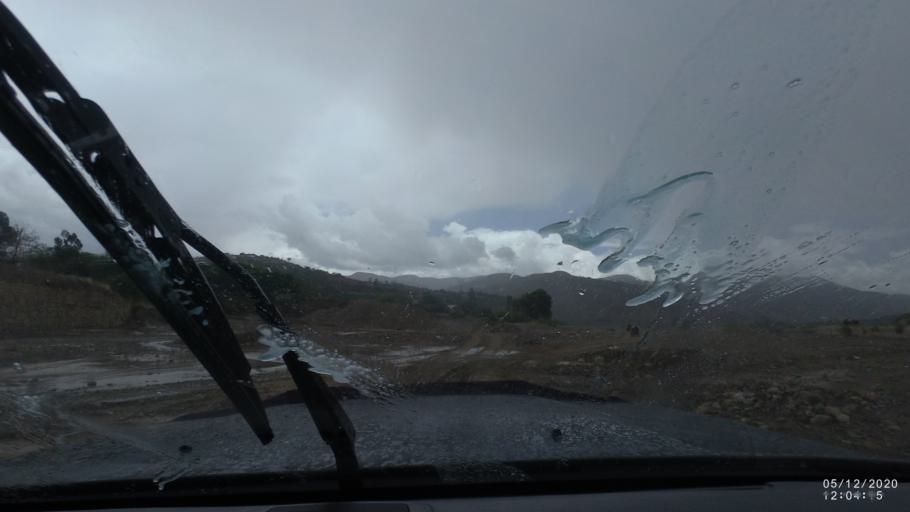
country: BO
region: Cochabamba
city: Sipe Sipe
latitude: -17.5714
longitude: -66.3558
